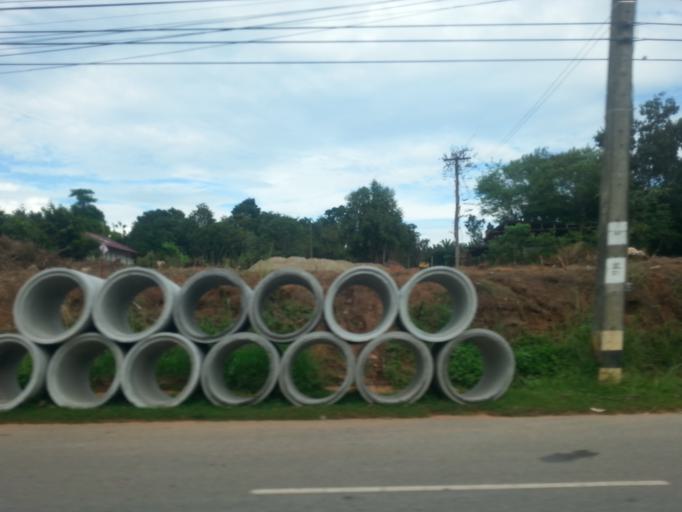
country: TH
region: Krabi
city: Krabi
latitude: 8.0896
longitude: 98.8924
